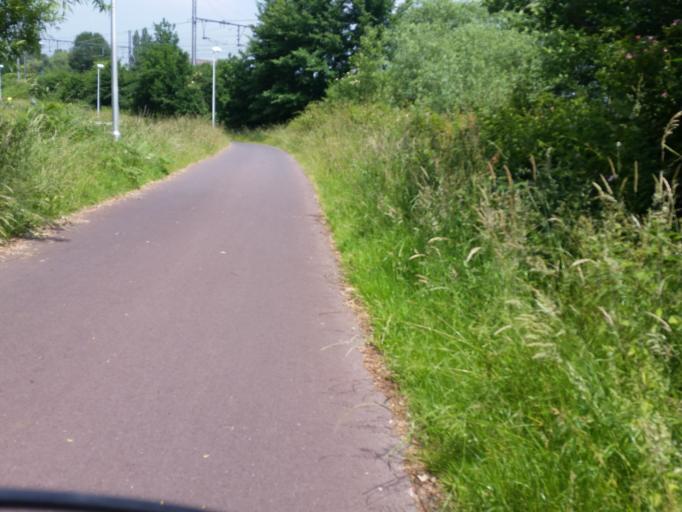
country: BE
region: Flanders
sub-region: Provincie Antwerpen
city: Hove
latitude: 51.1386
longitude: 4.4733
